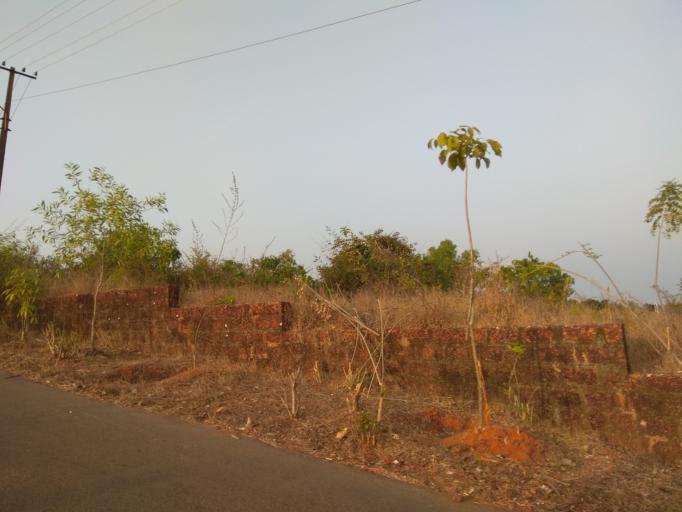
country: IN
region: Karnataka
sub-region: Dakshina Kannada
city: Mangalore
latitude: 12.9142
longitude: 74.8597
